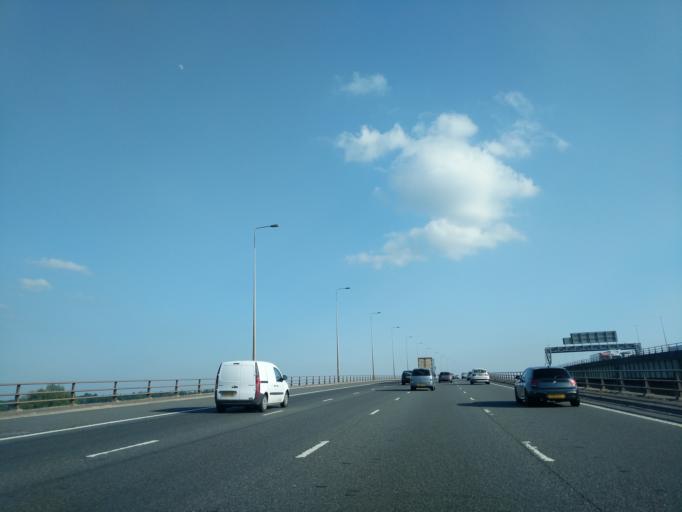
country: GB
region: England
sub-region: Warrington
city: Lymm
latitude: 53.3925
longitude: -2.5065
